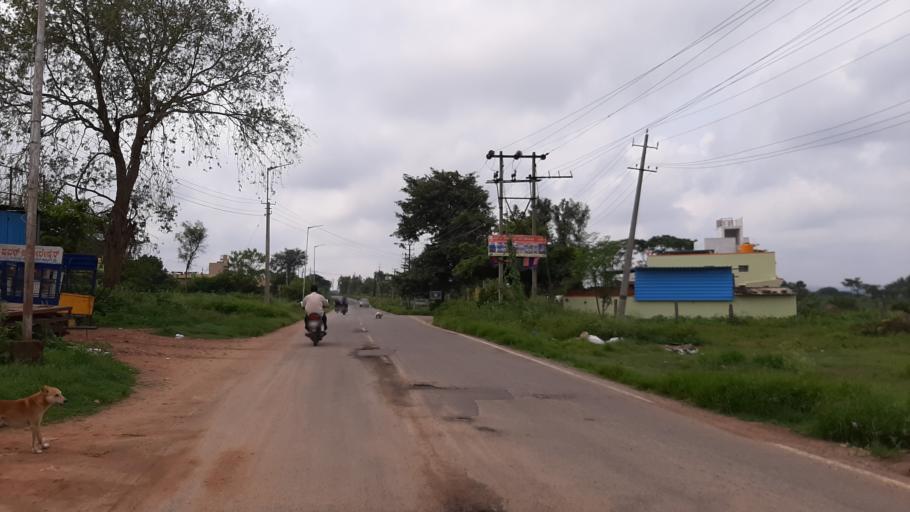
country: IN
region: Karnataka
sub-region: Ramanagara
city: Magadi
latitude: 12.9485
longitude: 77.2382
